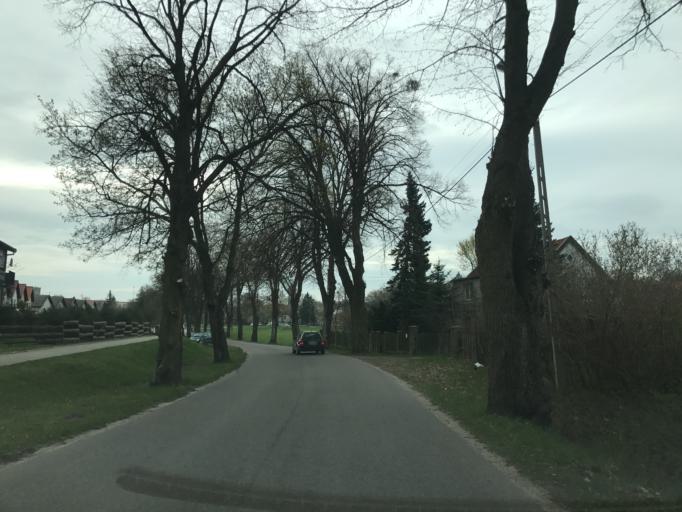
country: PL
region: Warmian-Masurian Voivodeship
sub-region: Powiat olsztynski
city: Olsztynek
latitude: 53.5872
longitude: 20.2816
